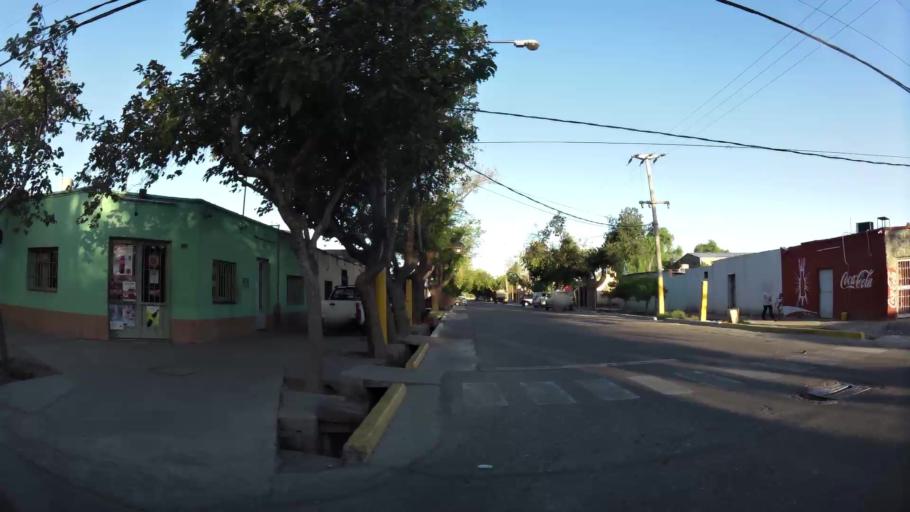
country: AR
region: San Juan
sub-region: Departamento de Santa Lucia
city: Santa Lucia
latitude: -31.5405
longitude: -68.4940
